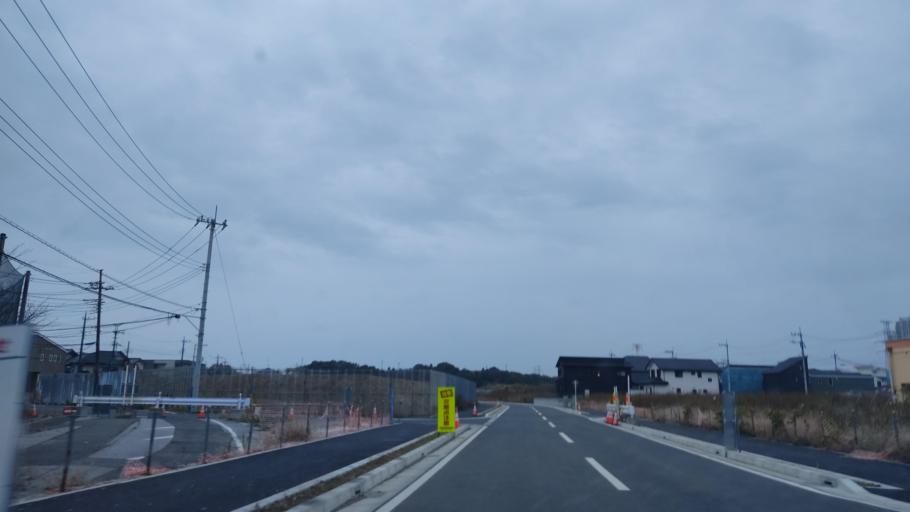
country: JP
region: Chiba
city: Kashiwa
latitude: 35.9036
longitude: 139.9563
